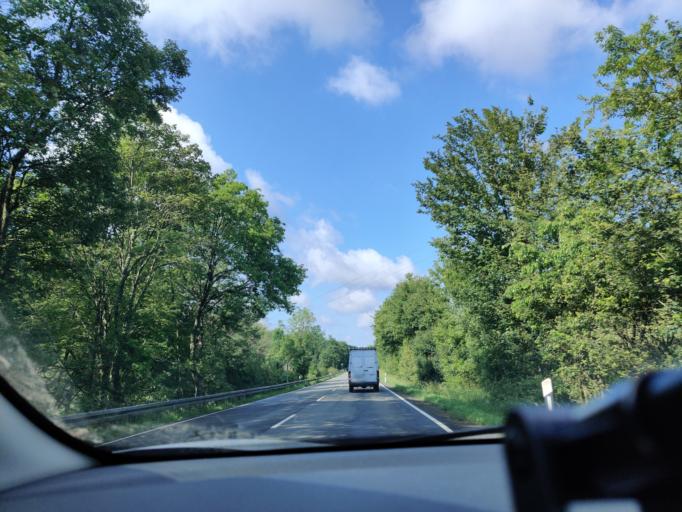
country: FR
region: Lorraine
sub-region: Departement de la Moselle
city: Bliesbruck
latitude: 49.1417
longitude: 7.1482
